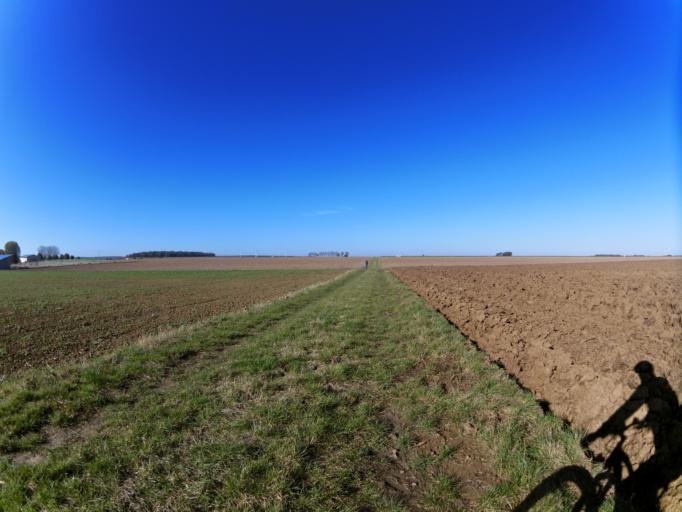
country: DE
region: Bavaria
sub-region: Regierungsbezirk Unterfranken
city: Giebelstadt
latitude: 49.6620
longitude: 9.9336
